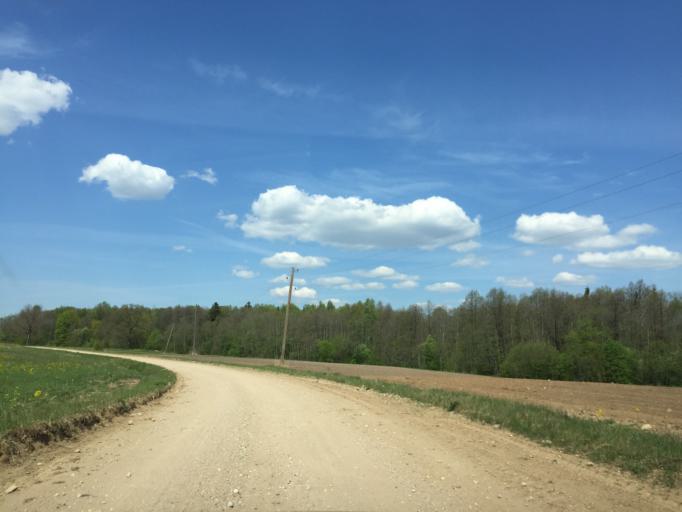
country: LV
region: Limbazu Rajons
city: Limbazi
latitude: 57.3782
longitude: 24.6268
